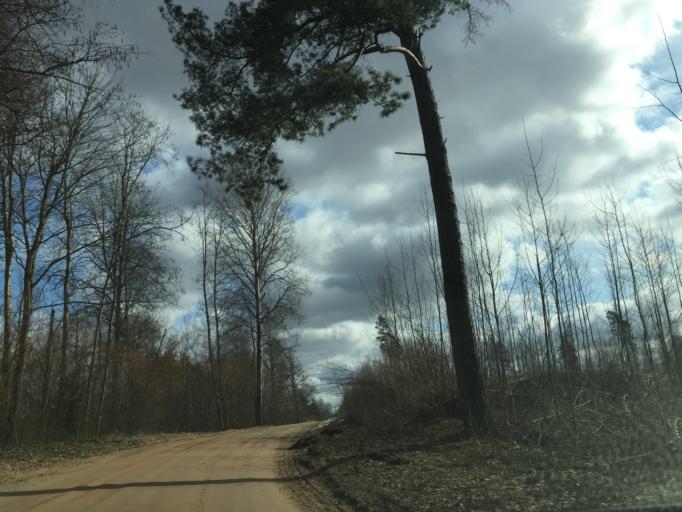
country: LV
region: Vecumnieki
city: Vecumnieki
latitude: 56.5859
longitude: 24.5760
